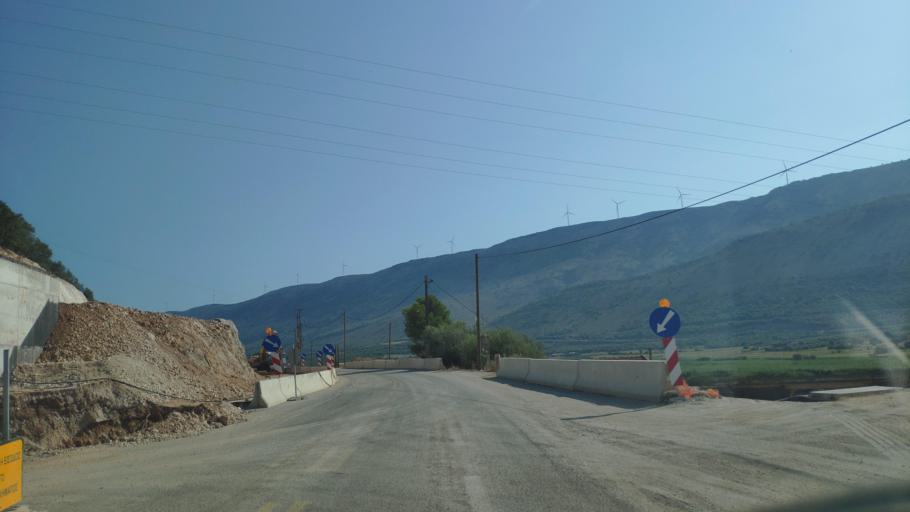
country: GR
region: West Greece
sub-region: Nomos Aitolias kai Akarnanias
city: Stanos
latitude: 38.7782
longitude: 21.1852
